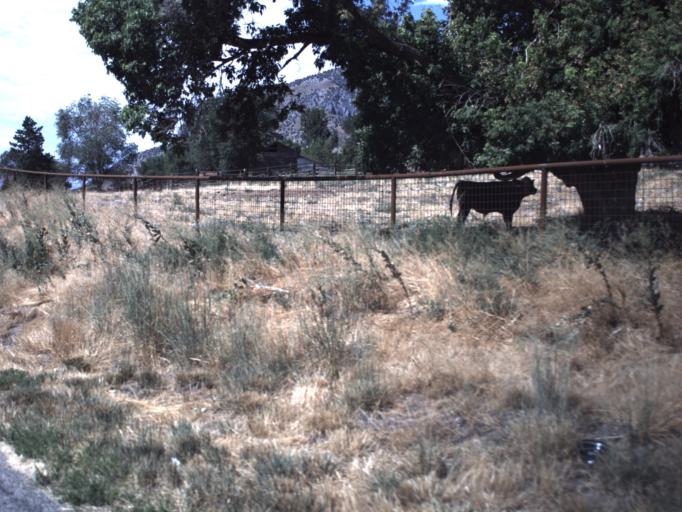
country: US
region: Utah
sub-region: Box Elder County
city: Honeyville
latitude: 41.5877
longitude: -112.0421
